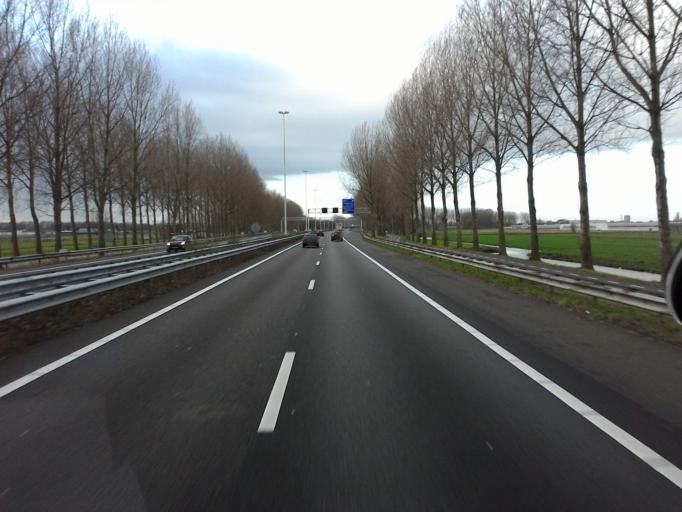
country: NL
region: South Holland
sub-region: Gemeente Waddinxveen
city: Waddinxveen
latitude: 51.9857
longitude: 4.6283
